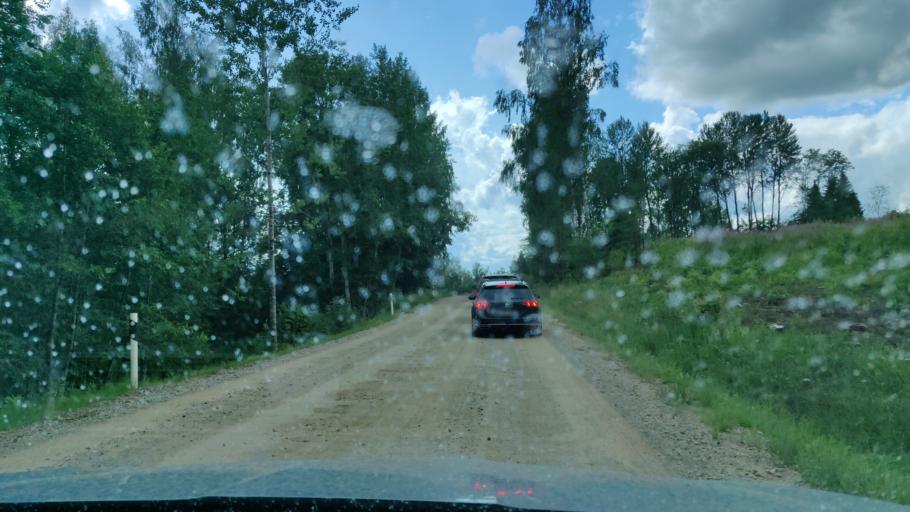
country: EE
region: Vorumaa
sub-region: Antsla vald
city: Vana-Antsla
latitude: 58.0156
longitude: 26.5761
